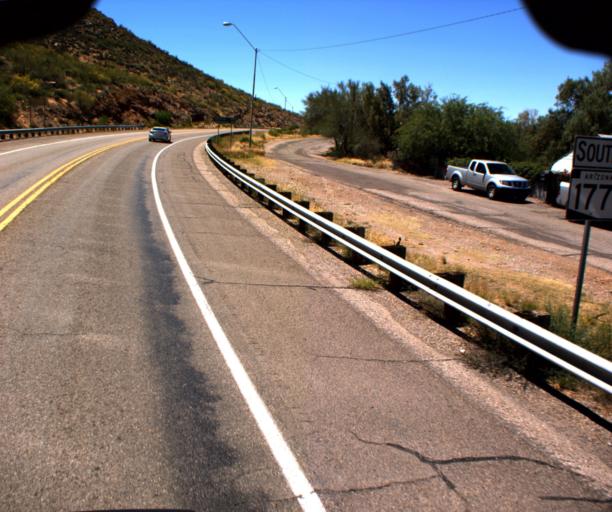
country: US
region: Arizona
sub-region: Pinal County
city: Superior
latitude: 33.2902
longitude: -111.0965
